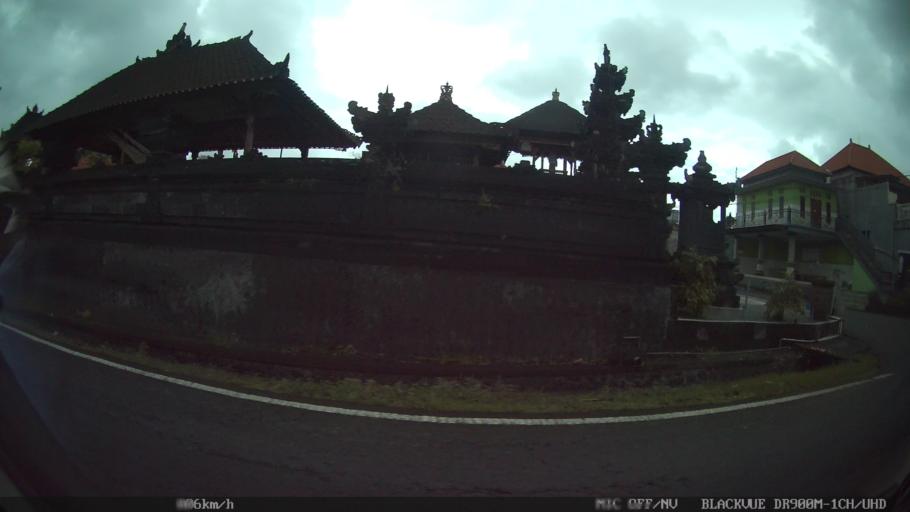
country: ID
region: Bali
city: Banjar Sempidi
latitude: -8.5232
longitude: 115.1963
